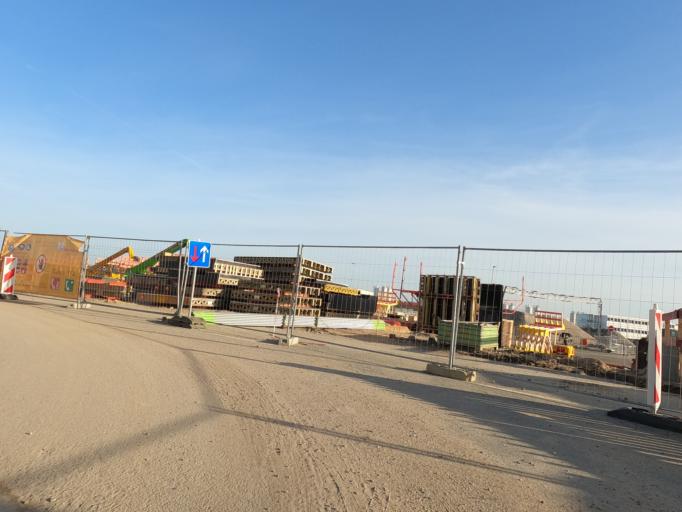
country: DE
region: Hesse
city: Morfelden-Walldorf
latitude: 50.0305
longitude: 8.5866
